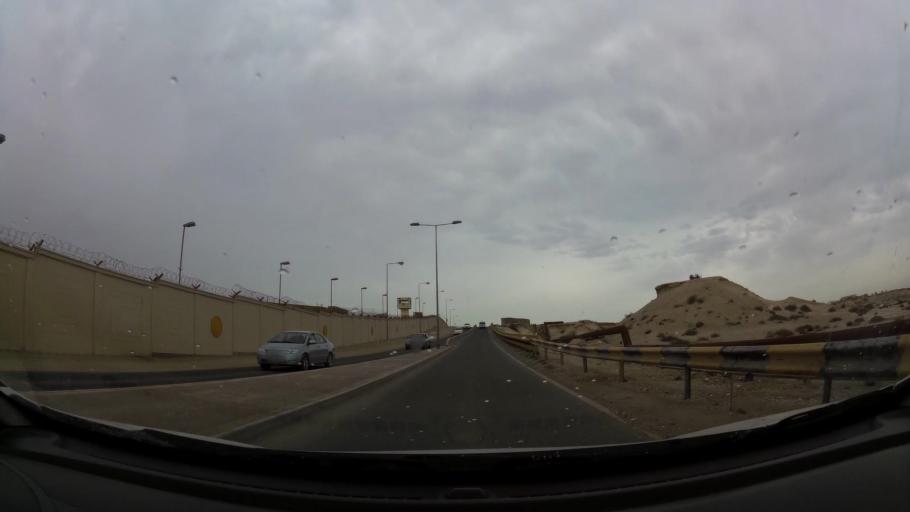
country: BH
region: Central Governorate
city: Madinat Hamad
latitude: 26.1511
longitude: 50.4851
